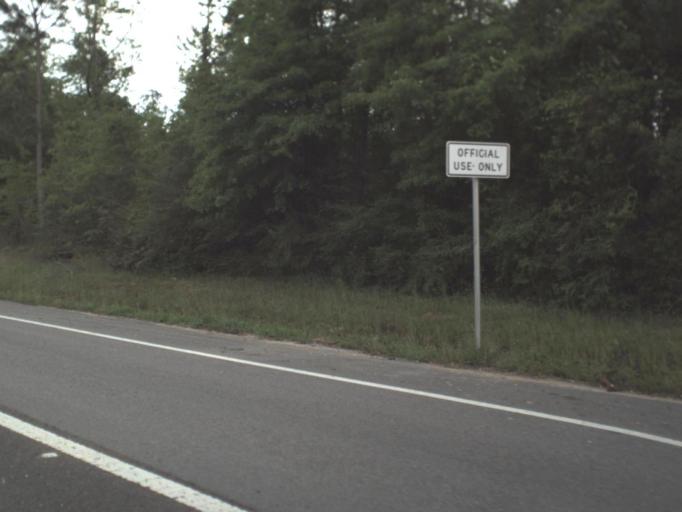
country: US
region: Florida
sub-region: Escambia County
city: Cantonment
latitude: 30.6376
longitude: -87.3402
